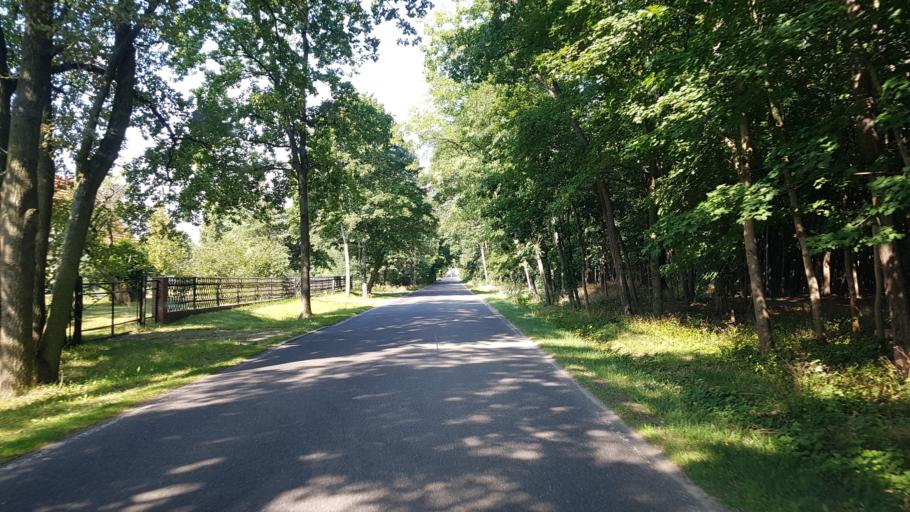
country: DE
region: Brandenburg
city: Vetschau
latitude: 51.7762
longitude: 14.0940
